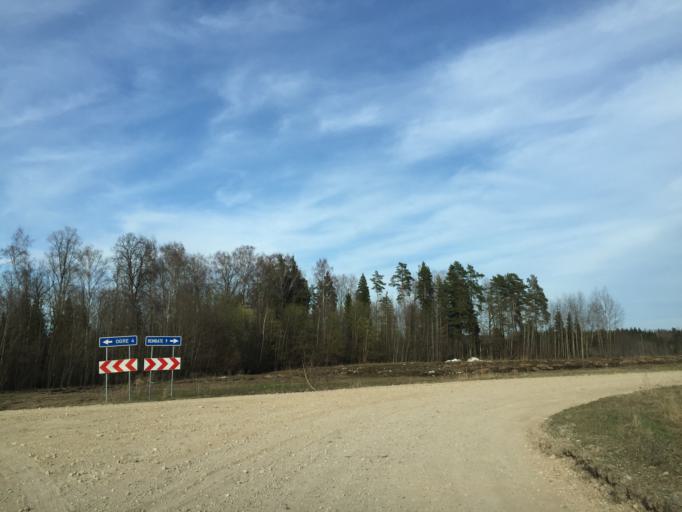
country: LV
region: Kegums
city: Kegums
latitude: 56.7927
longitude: 24.7111
